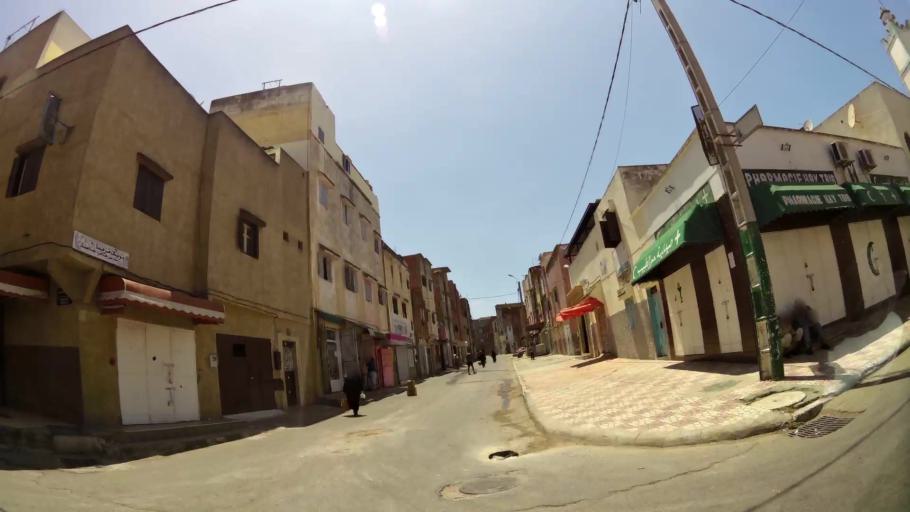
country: MA
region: Gharb-Chrarda-Beni Hssen
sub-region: Kenitra Province
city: Kenitra
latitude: 34.2558
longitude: -6.5522
